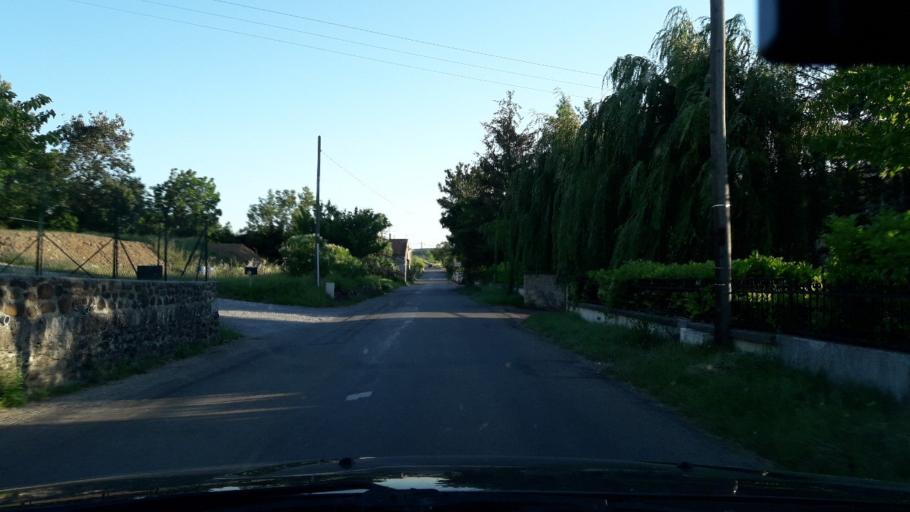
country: FR
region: Rhone-Alpes
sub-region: Departement de l'Ardeche
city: Lavilledieu
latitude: 44.6075
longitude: 4.4716
